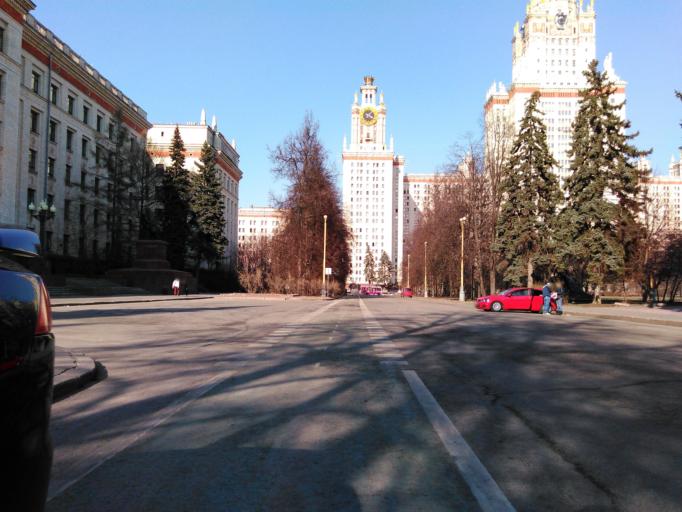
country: RU
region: Moscow
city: Vorob'yovo
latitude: 55.7017
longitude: 37.5261
